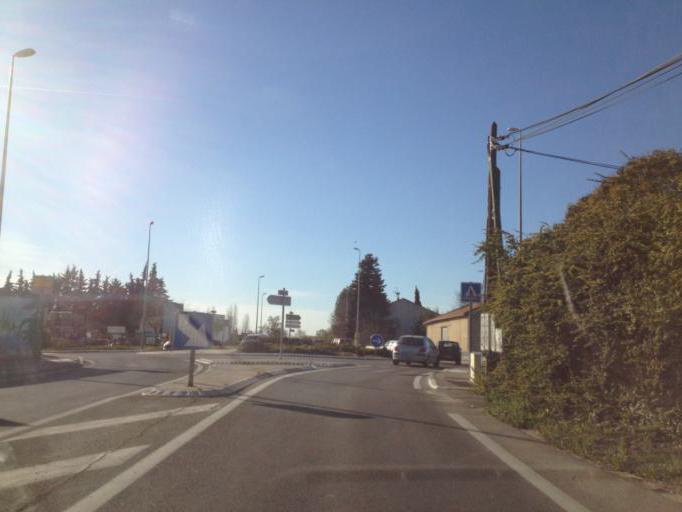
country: FR
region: Provence-Alpes-Cote d'Azur
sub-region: Departement des Bouches-du-Rhone
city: Saint-Cannat
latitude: 43.6121
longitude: 5.3250
